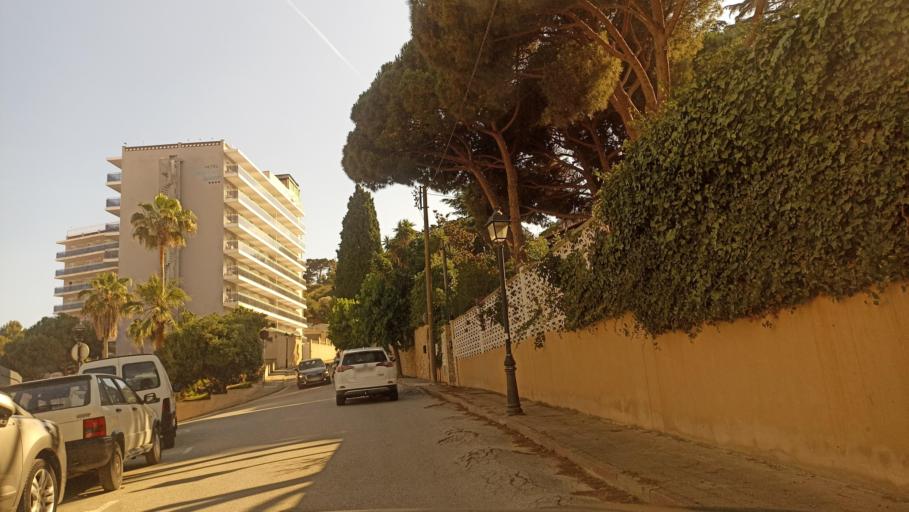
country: ES
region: Catalonia
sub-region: Provincia de Barcelona
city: Calella
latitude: 41.6140
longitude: 2.6501
